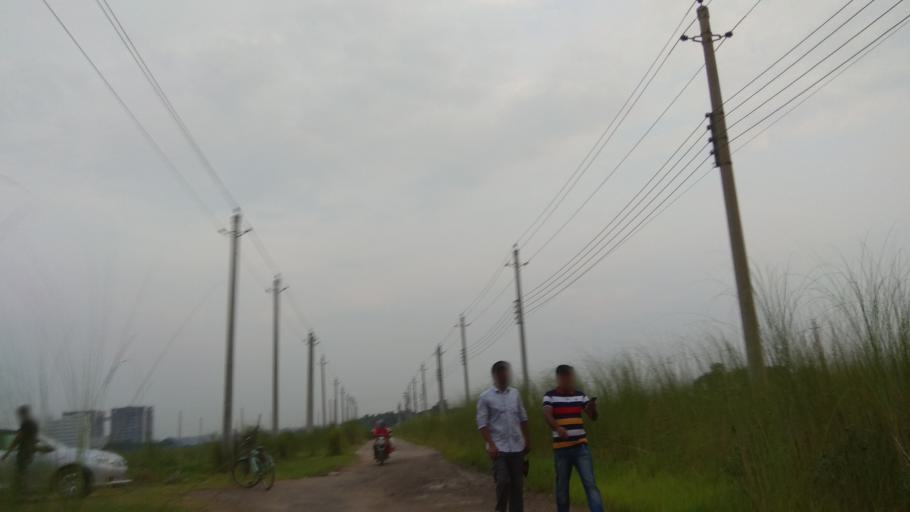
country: BD
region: Dhaka
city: Tungi
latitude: 23.8559
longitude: 90.3688
